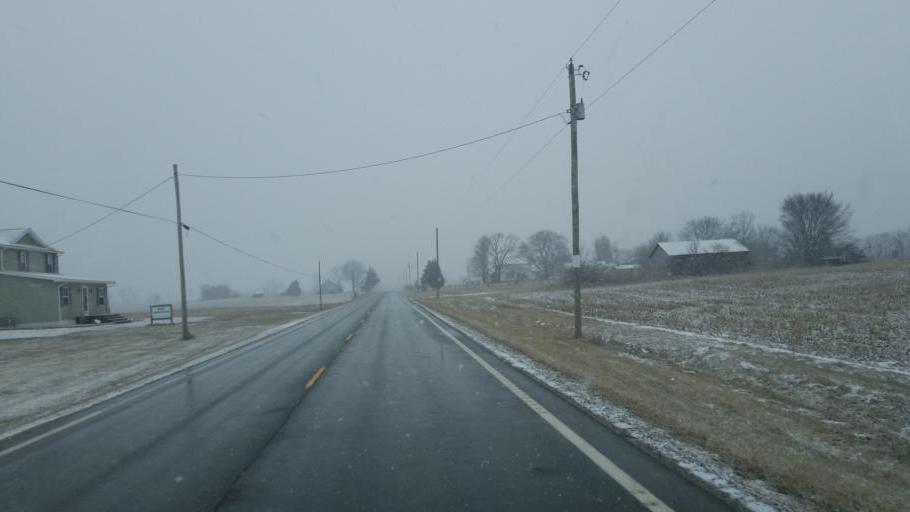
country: US
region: Ohio
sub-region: Defiance County
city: Hicksville
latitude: 41.3413
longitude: -84.7477
